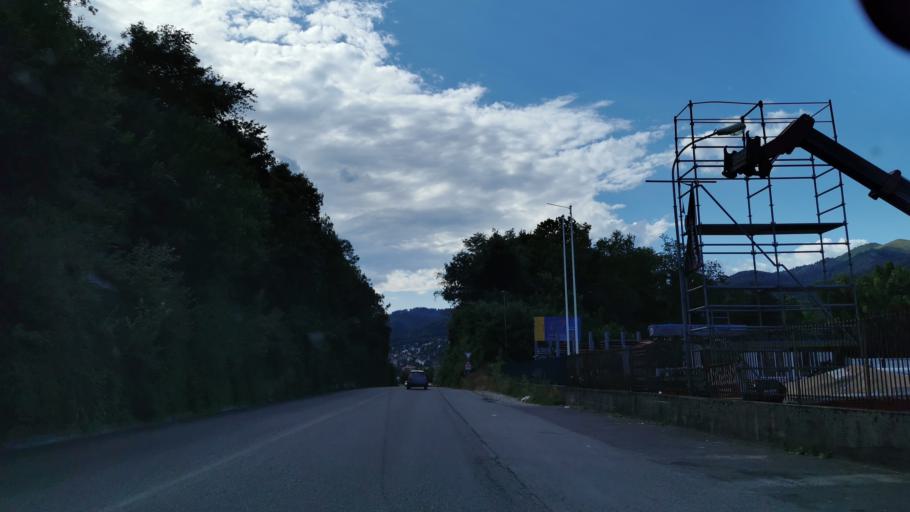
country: IT
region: Lombardy
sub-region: Provincia di Como
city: Albese Con Cassano
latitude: 45.7917
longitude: 9.1540
